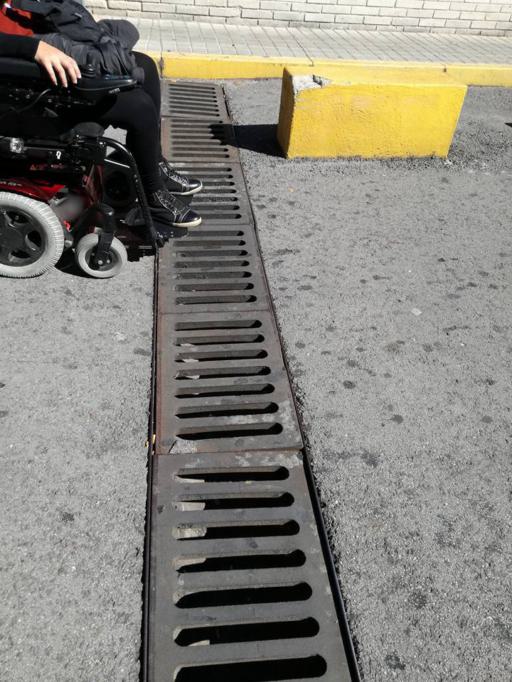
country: ES
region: Madrid
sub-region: Provincia de Madrid
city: Salamanca
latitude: 40.4194
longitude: -3.6693
